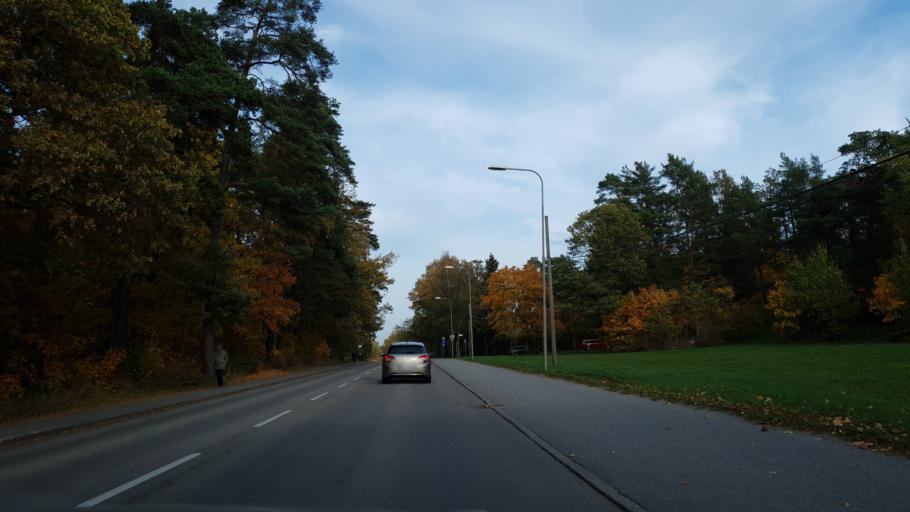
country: SE
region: Stockholm
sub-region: Stockholms Kommun
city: Bromma
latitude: 59.3417
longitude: 17.8880
